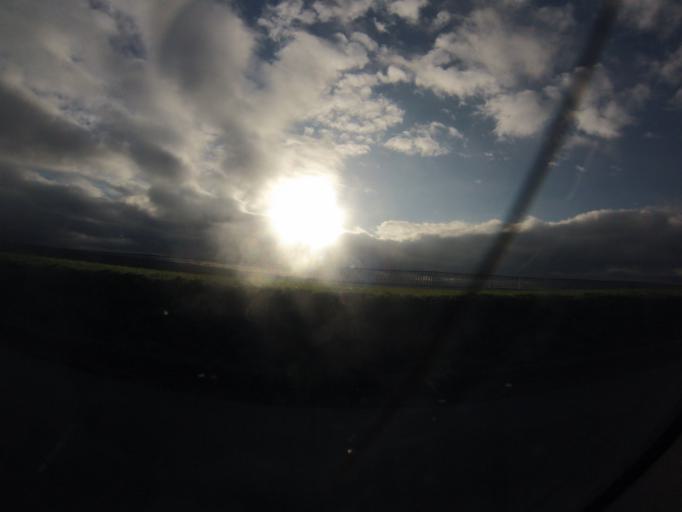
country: DE
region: Thuringia
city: Vollmershain
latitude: 50.8578
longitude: 12.3062
